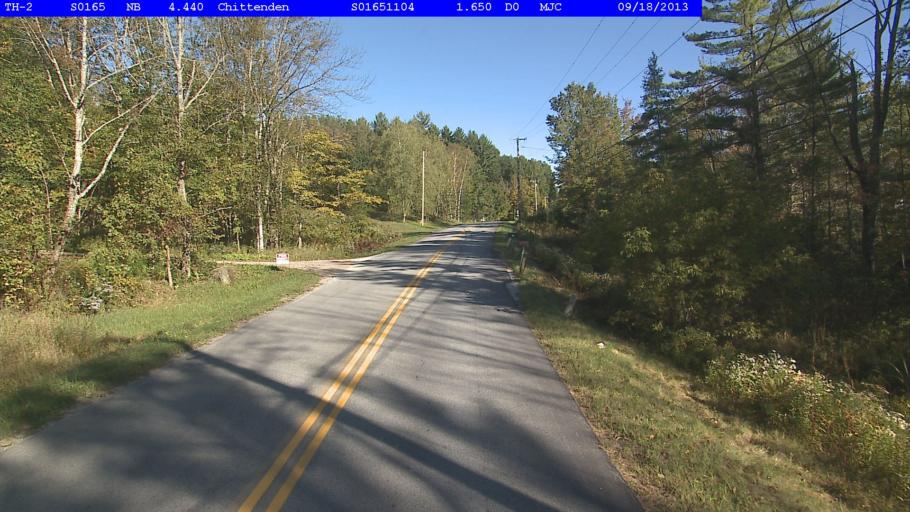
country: US
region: Vermont
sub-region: Rutland County
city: Rutland
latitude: 43.6995
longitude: -72.9590
